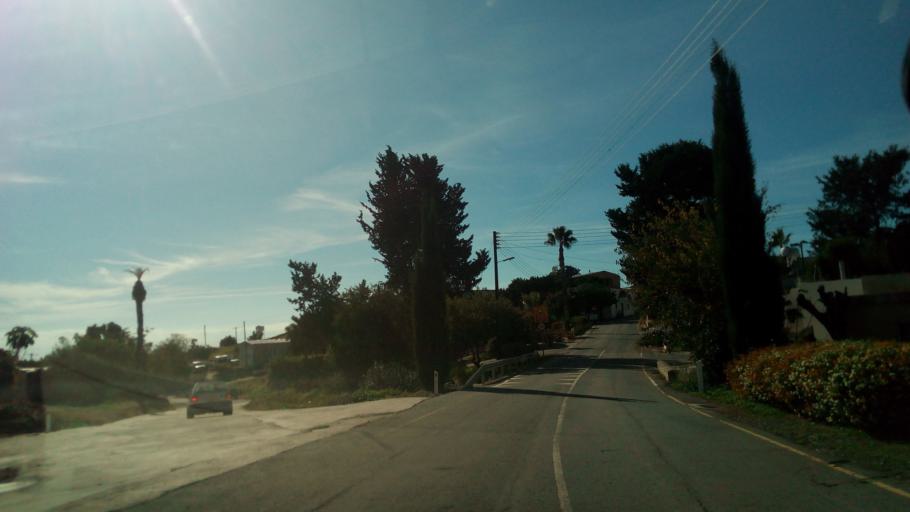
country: CY
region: Limassol
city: Pissouri
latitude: 34.7088
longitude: 32.5771
